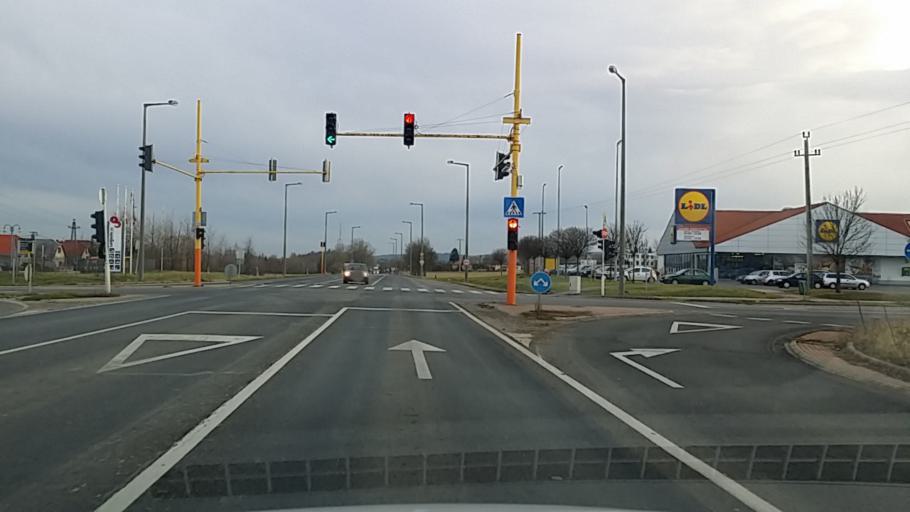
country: HU
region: Fejer
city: Mor
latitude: 47.3764
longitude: 18.1906
